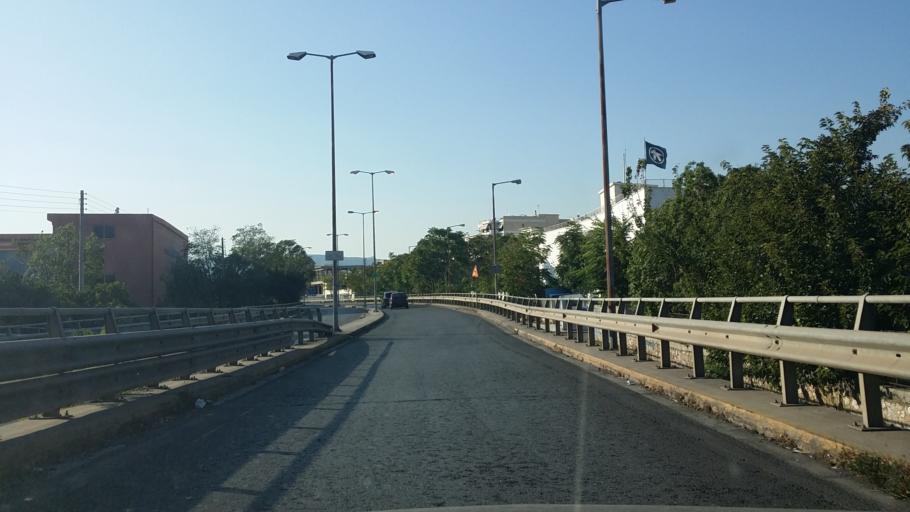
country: GR
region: Attica
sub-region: Nomarchia Athinas
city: Agioi Anargyroi
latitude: 38.0142
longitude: 23.7171
